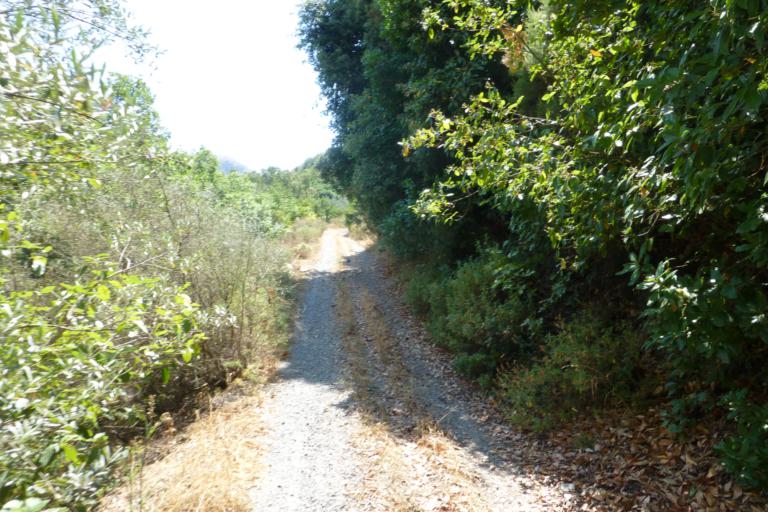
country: IT
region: Calabria
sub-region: Provincia di Reggio Calabria
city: Pazzano
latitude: 38.4809
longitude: 16.4394
